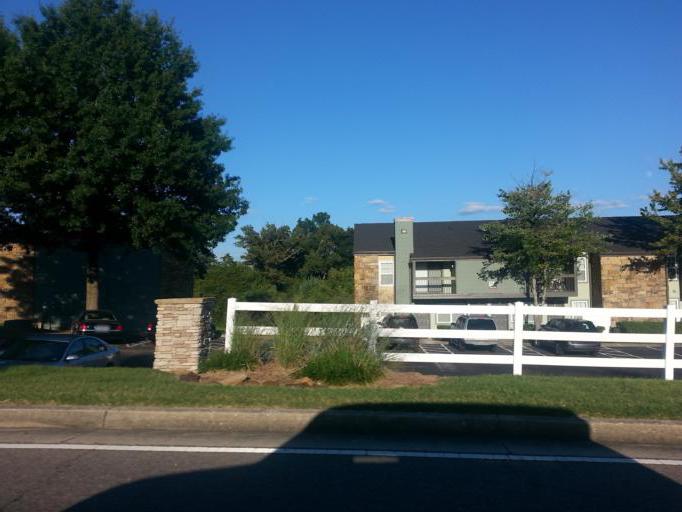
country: US
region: Tennessee
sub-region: Knox County
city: Farragut
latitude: 35.9327
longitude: -84.0950
